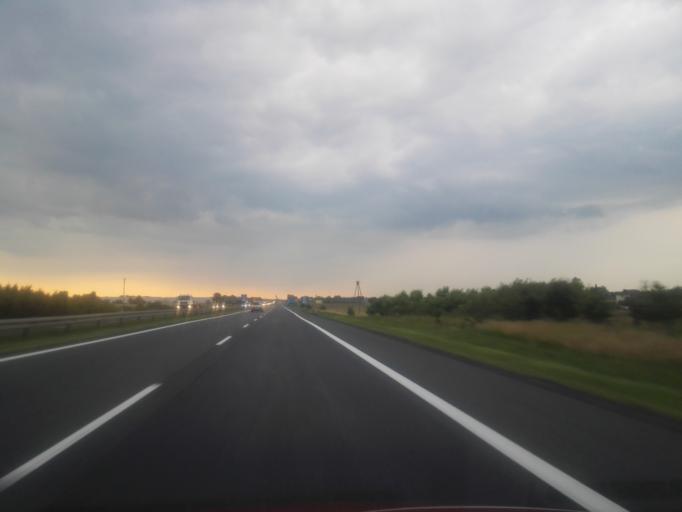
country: PL
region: Lodz Voivodeship
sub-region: Piotrkow Trybunalski
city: Piotrkow Trybunalski
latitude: 51.3978
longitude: 19.6310
